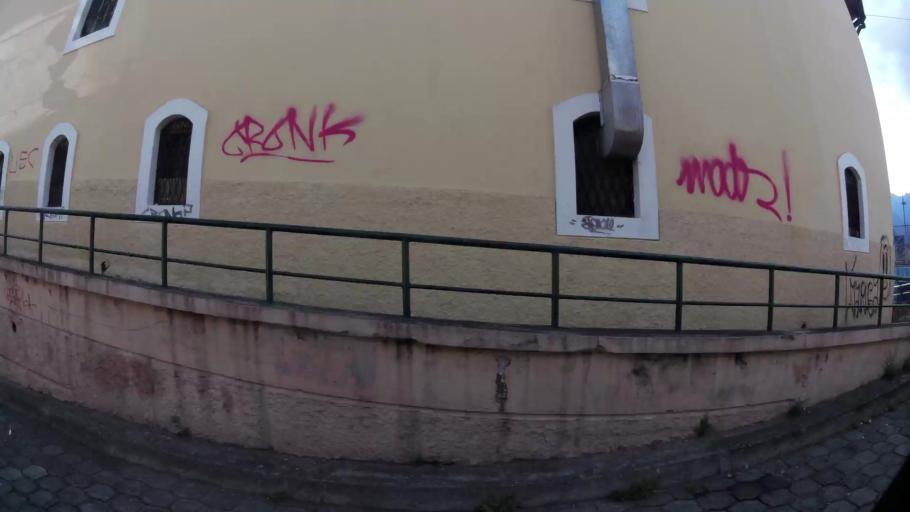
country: EC
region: Pichincha
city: Quito
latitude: -0.2228
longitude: -78.5042
